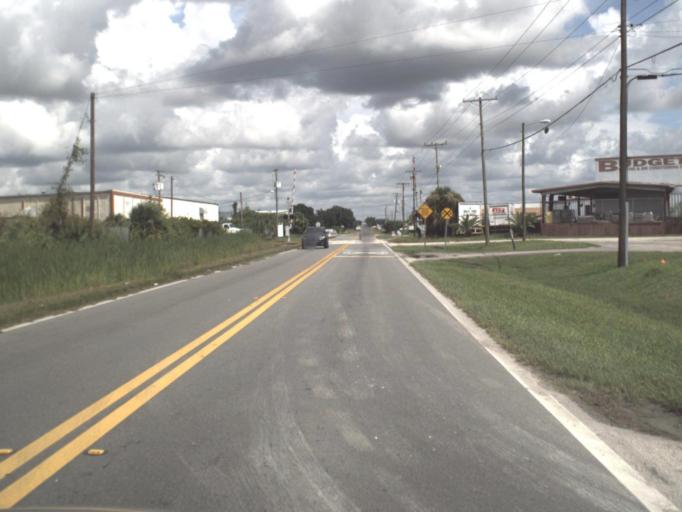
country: US
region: Florida
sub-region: Hillsborough County
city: Egypt Lake-Leto
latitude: 28.0046
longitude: -82.5289
